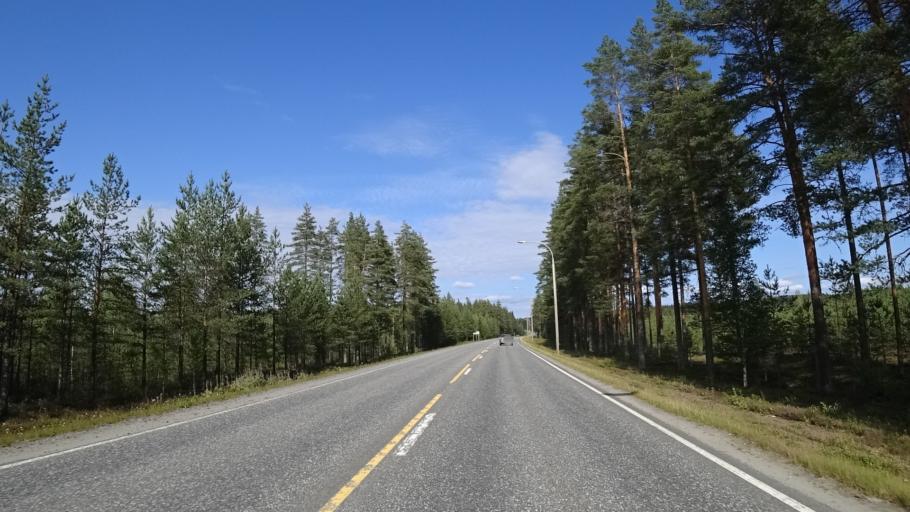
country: FI
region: North Karelia
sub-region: Joensuu
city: Eno
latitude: 62.7731
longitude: 30.0528
